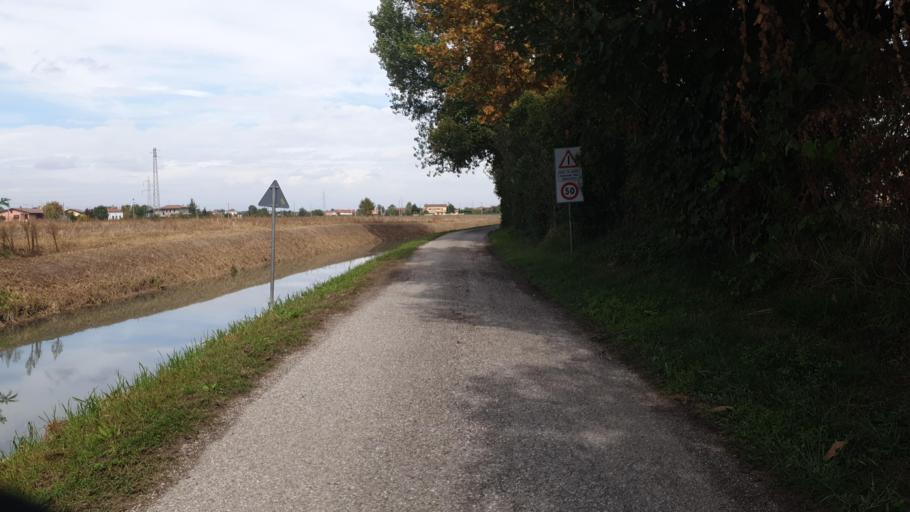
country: IT
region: Veneto
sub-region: Provincia di Padova
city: Polverara
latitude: 45.2978
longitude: 11.9631
